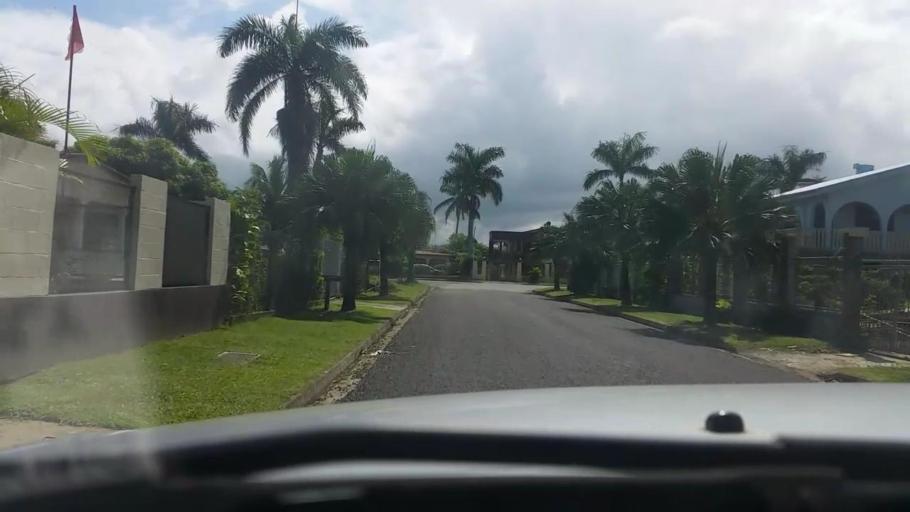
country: FJ
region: Central
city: Suva
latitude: -18.1304
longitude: 178.4651
